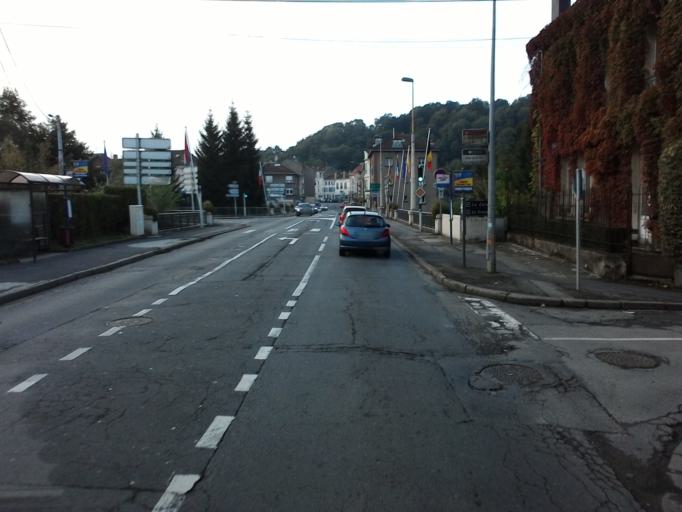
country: FR
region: Lorraine
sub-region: Departement de Meurthe-et-Moselle
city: Longuyon
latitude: 49.4489
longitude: 5.5997
